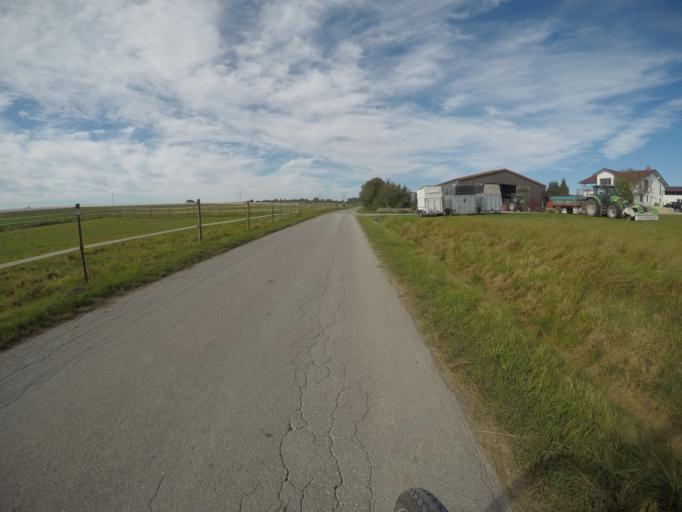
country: DE
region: Baden-Wuerttemberg
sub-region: Regierungsbezirk Stuttgart
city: Ehningen
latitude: 48.6563
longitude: 8.9223
